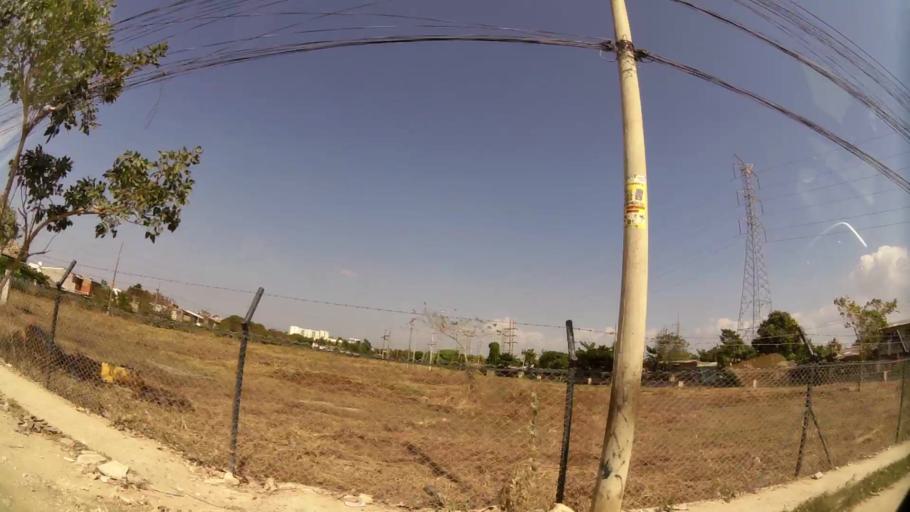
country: CO
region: Bolivar
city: Cartagena
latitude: 10.3763
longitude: -75.4660
